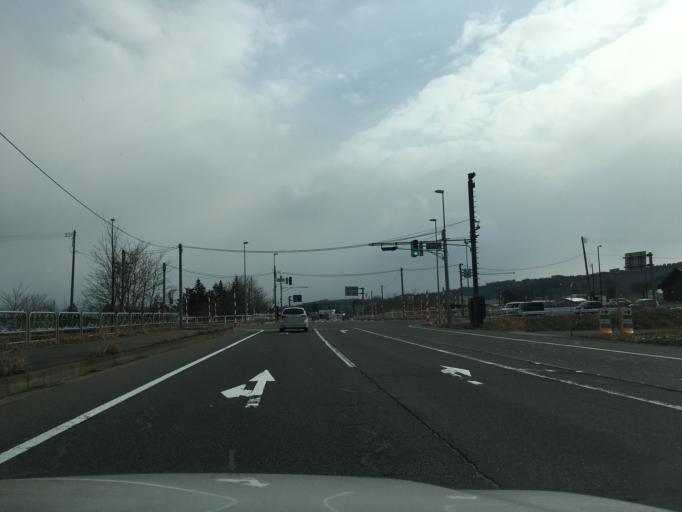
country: JP
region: Aomori
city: Namioka
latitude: 40.7601
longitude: 140.5870
